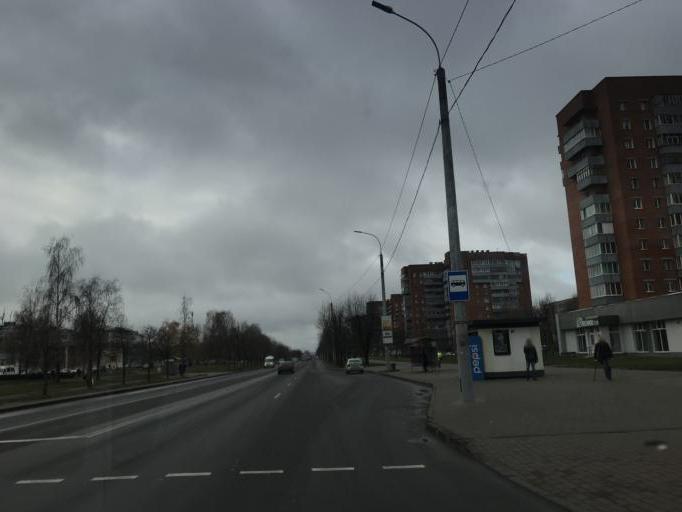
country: BY
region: Mogilev
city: Mahilyow
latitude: 53.8744
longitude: 30.3312
